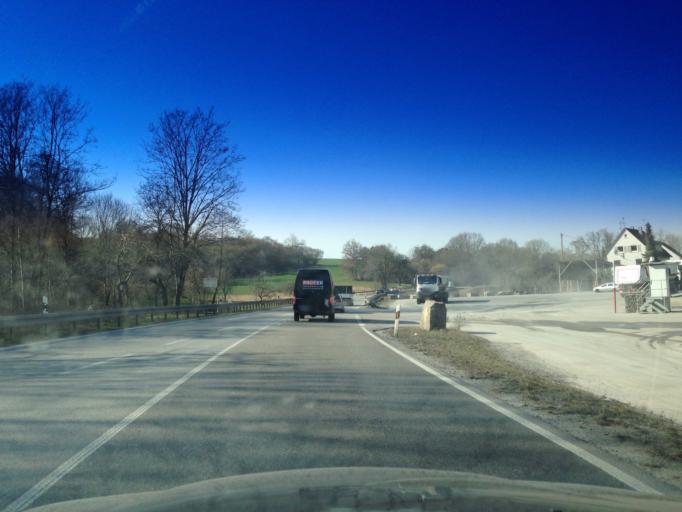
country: DE
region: Baden-Wuerttemberg
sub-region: Karlsruhe Region
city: Illingen
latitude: 48.9434
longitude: 8.9376
